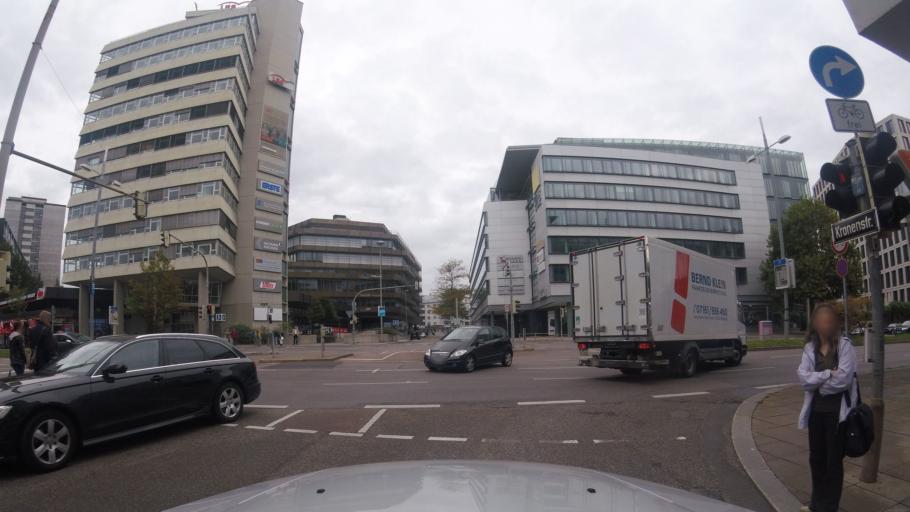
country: DE
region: Baden-Wuerttemberg
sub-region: Regierungsbezirk Stuttgart
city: Stuttgart
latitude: 48.7830
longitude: 9.1778
